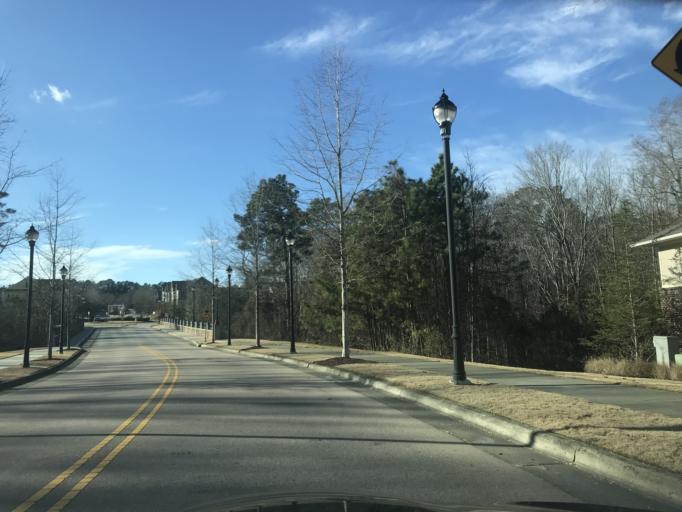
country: US
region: North Carolina
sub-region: Wake County
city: Cary
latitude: 35.8092
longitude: -78.7326
